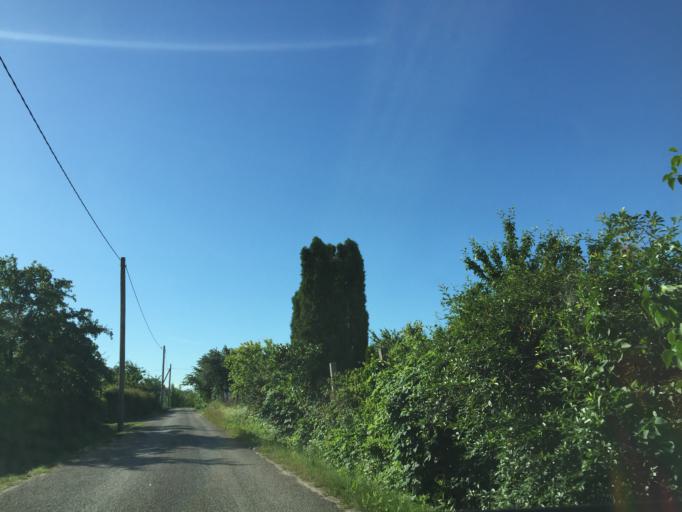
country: LV
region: Ventspils
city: Ventspils
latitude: 57.3698
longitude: 21.6072
